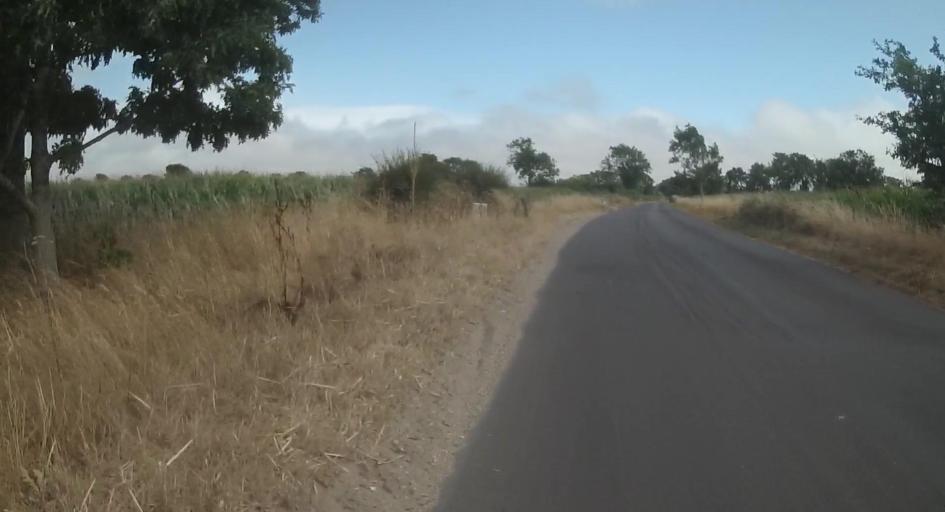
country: GB
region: England
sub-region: Dorset
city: Bovington Camp
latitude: 50.6991
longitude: -2.2747
